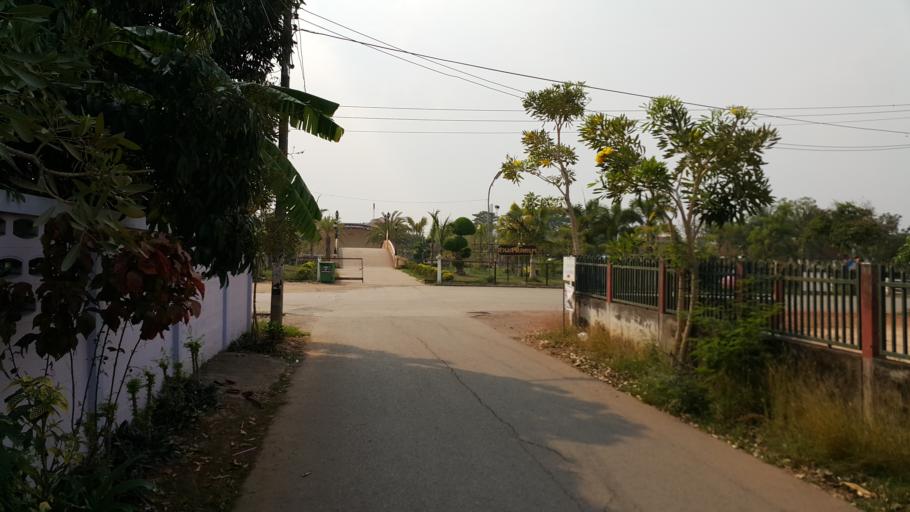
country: TH
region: Nakhon Phanom
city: That Phanom
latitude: 16.9464
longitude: 104.7280
